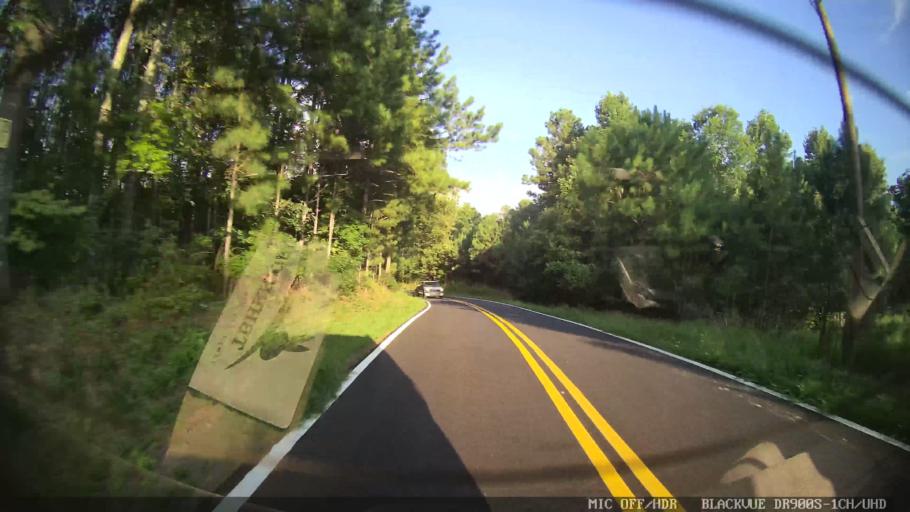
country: US
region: Georgia
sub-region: Bartow County
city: Emerson
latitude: 34.2036
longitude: -84.6833
